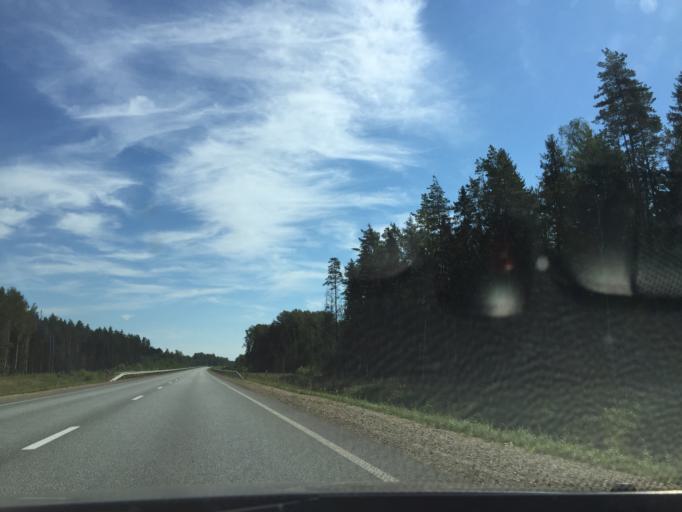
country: LV
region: Aizkraukles Rajons
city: Aizkraukle
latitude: 56.6991
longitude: 25.3172
